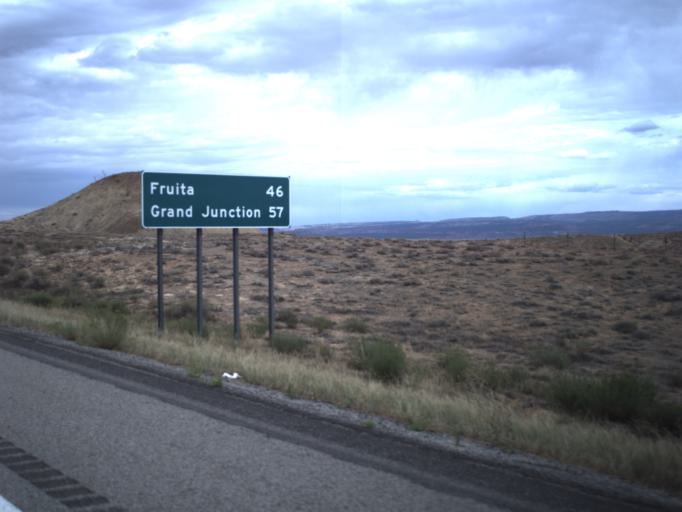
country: US
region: Utah
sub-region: Grand County
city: Moab
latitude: 38.9490
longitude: -109.3938
